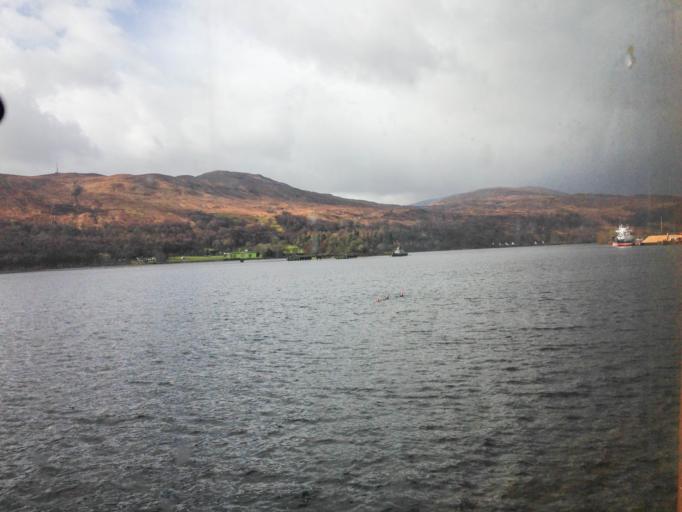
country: GB
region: Scotland
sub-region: Highland
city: Fort William
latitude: 56.8430
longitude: -5.1265
